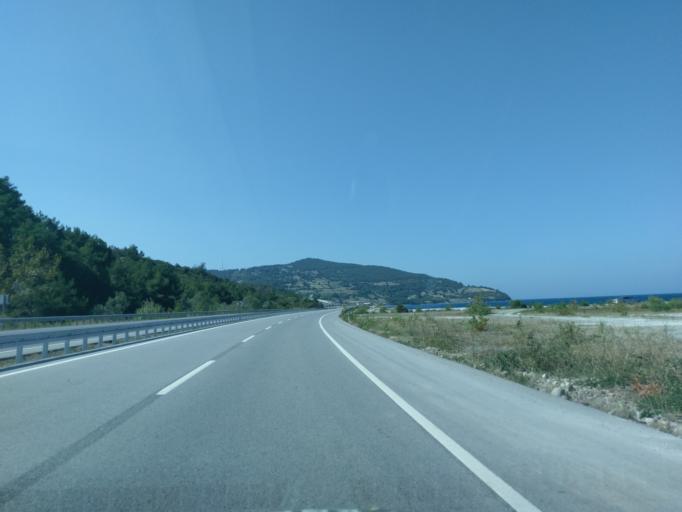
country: TR
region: Sinop
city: Dikmen
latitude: 41.7167
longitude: 35.2752
